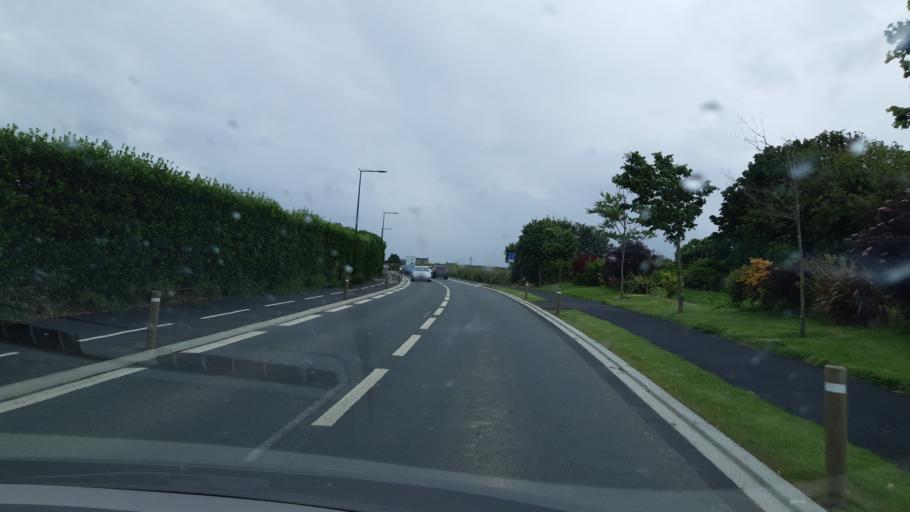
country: FR
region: Brittany
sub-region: Departement du Finistere
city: Roscoff
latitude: 48.7124
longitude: -3.9848
